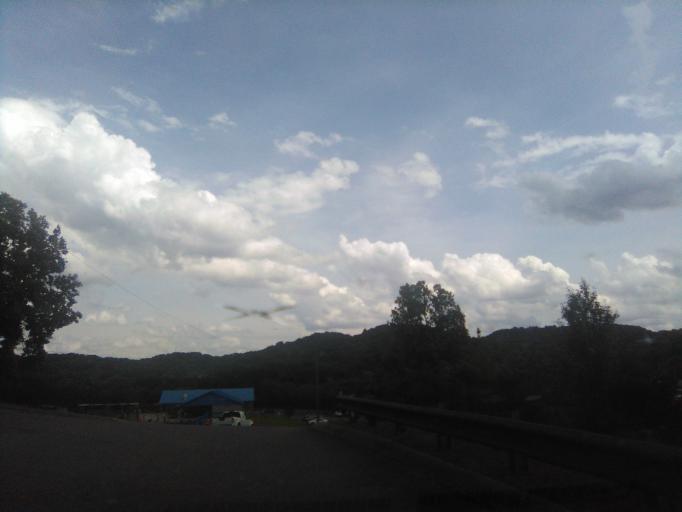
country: US
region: Tennessee
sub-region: Davidson County
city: Belle Meade
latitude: 36.0847
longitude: -86.8892
